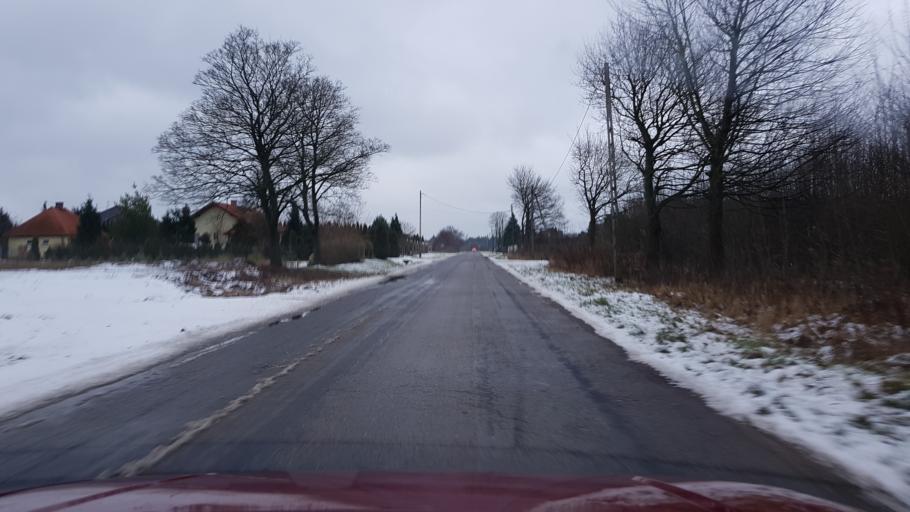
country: PL
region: West Pomeranian Voivodeship
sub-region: Powiat goleniowski
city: Nowogard
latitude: 53.6493
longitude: 15.1232
